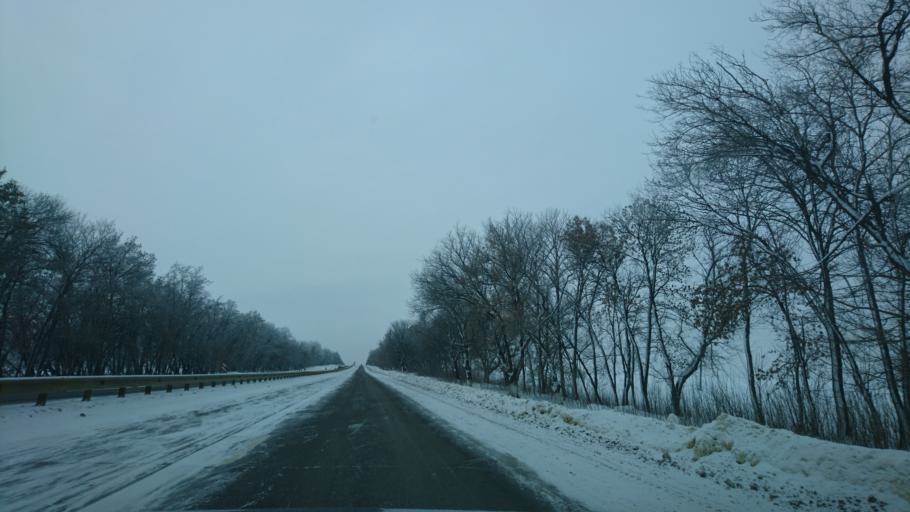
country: RU
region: Belgorod
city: Mayskiy
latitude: 50.4251
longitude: 36.3811
